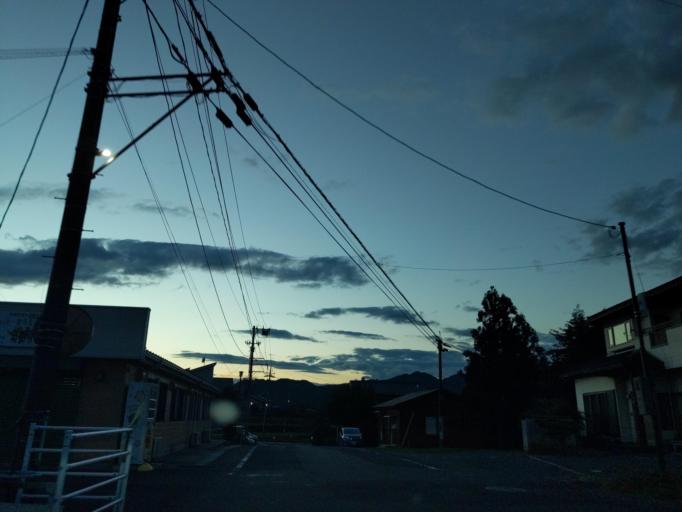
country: JP
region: Fukushima
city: Motomiya
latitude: 37.4974
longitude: 140.3862
